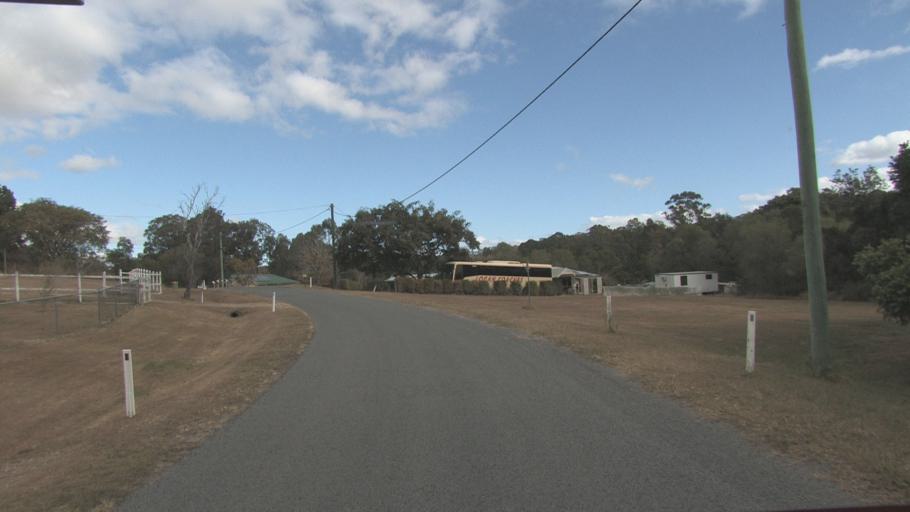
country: AU
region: Queensland
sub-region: Logan
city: Cedar Vale
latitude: -27.8747
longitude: 153.0142
